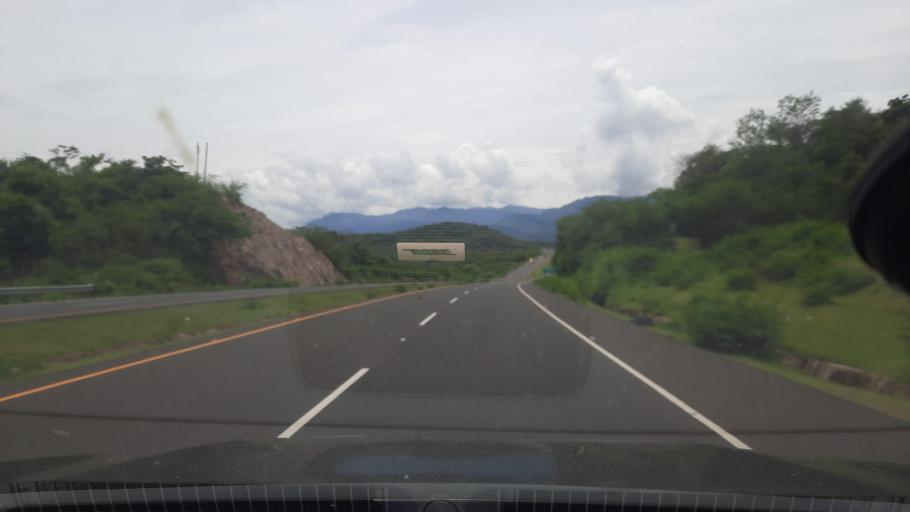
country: HN
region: Valle
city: Aramecina
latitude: 13.6823
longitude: -87.7283
